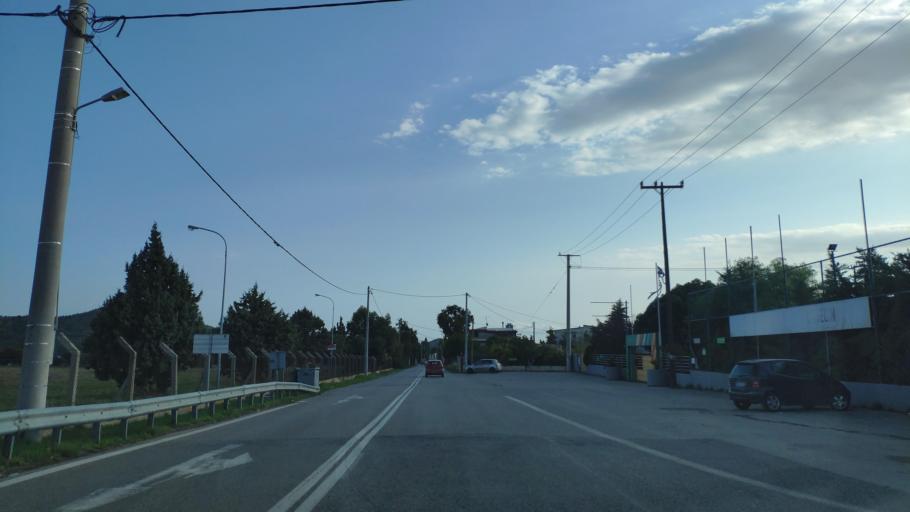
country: GR
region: Attica
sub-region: Nomarchia Dytikis Attikis
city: Megara
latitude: 37.9832
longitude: 23.3533
